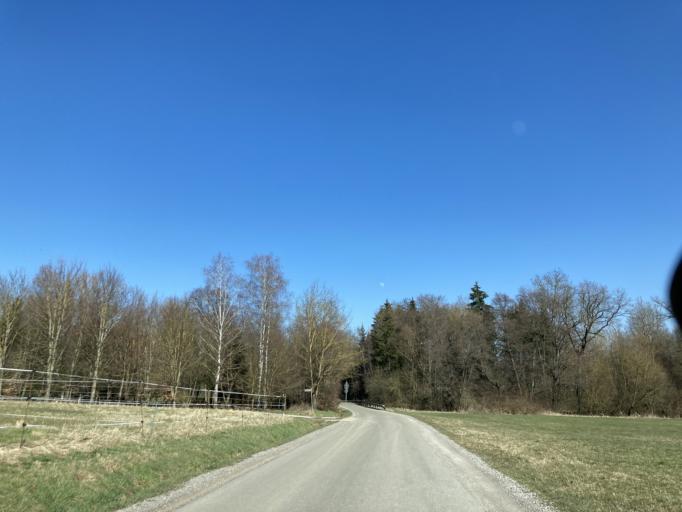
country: DE
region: Baden-Wuerttemberg
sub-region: Tuebingen Region
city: Bodelshausen
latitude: 48.4061
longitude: 8.9980
